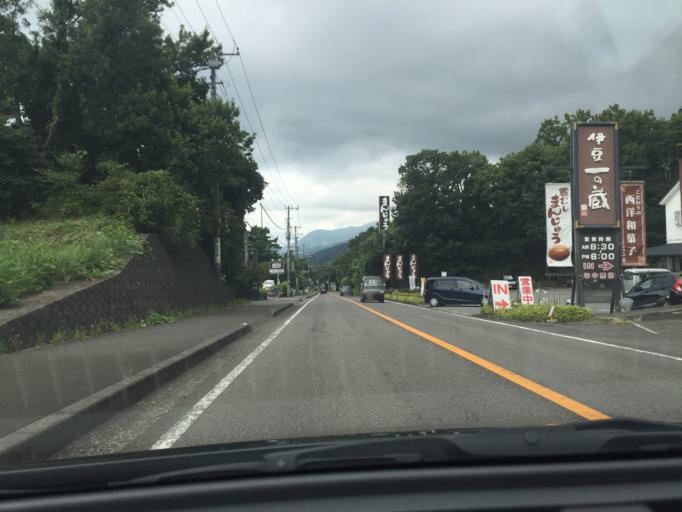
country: JP
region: Shizuoka
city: Ito
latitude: 34.8899
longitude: 139.1157
